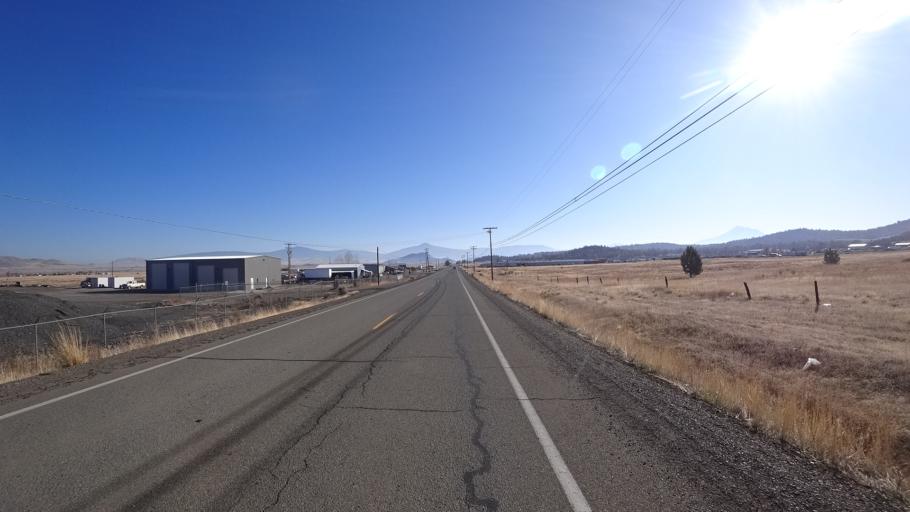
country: US
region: California
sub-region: Siskiyou County
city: Yreka
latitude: 41.7125
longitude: -122.6031
